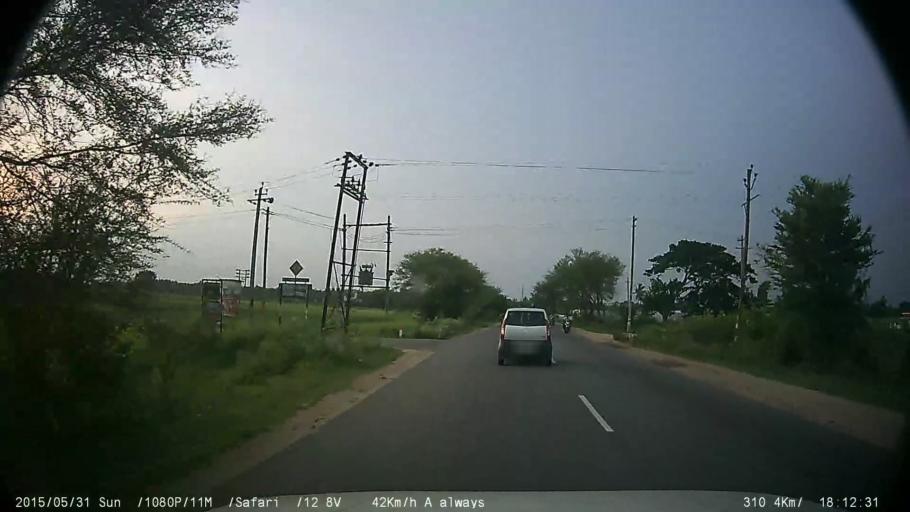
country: IN
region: Karnataka
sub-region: Mysore
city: Nanjangud
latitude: 12.0965
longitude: 76.6722
